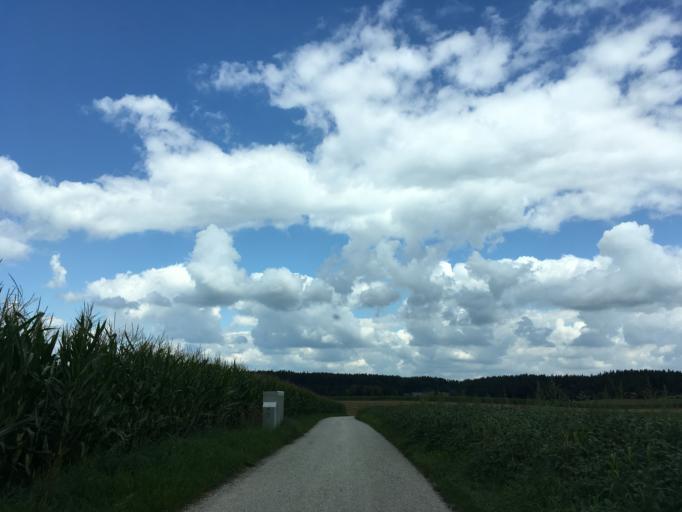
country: DE
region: Bavaria
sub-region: Upper Bavaria
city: Schnaitsee
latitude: 48.0467
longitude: 12.3370
